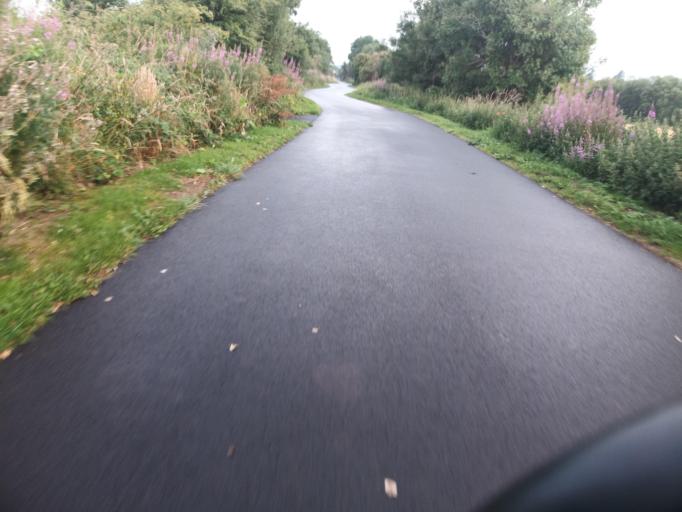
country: GB
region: Northern Ireland
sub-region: Castlereagh District
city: Dundonald
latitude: 54.5760
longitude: -5.7809
